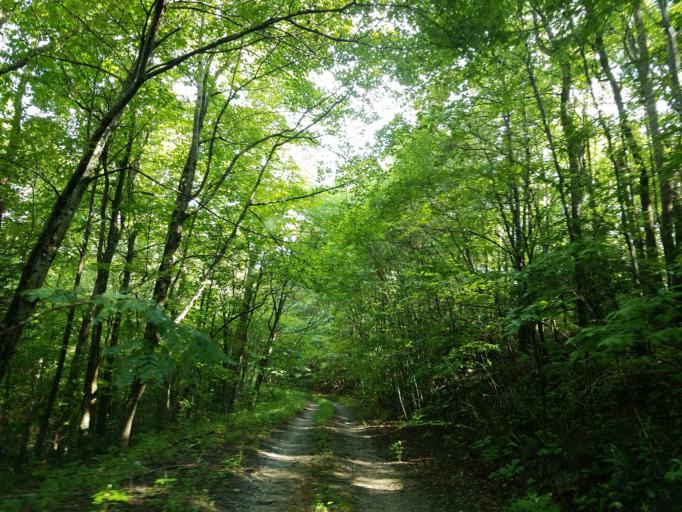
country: US
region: Georgia
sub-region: Fannin County
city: Blue Ridge
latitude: 34.6677
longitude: -84.2383
